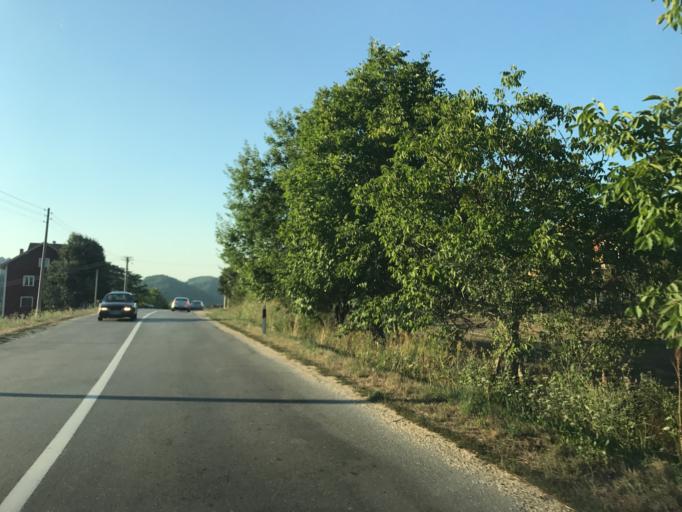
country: RO
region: Mehedinti
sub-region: Comuna Svinita
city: Svinita
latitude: 44.4058
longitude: 22.1731
